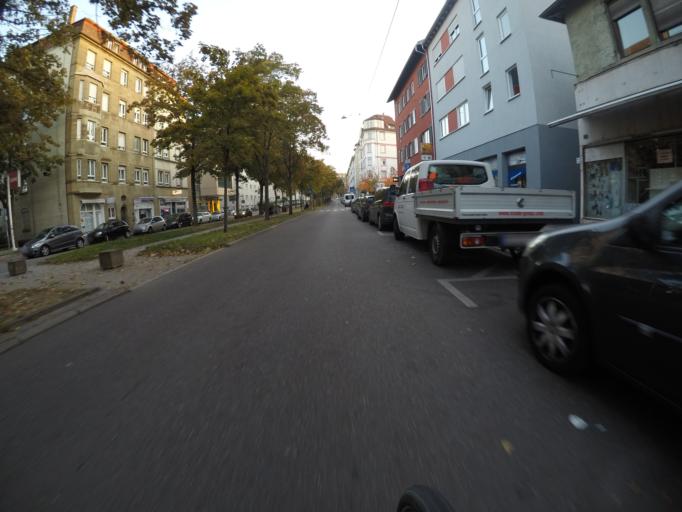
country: DE
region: Baden-Wuerttemberg
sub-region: Regierungsbezirk Stuttgart
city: Stuttgart-Ost
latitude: 48.7846
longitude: 9.2078
